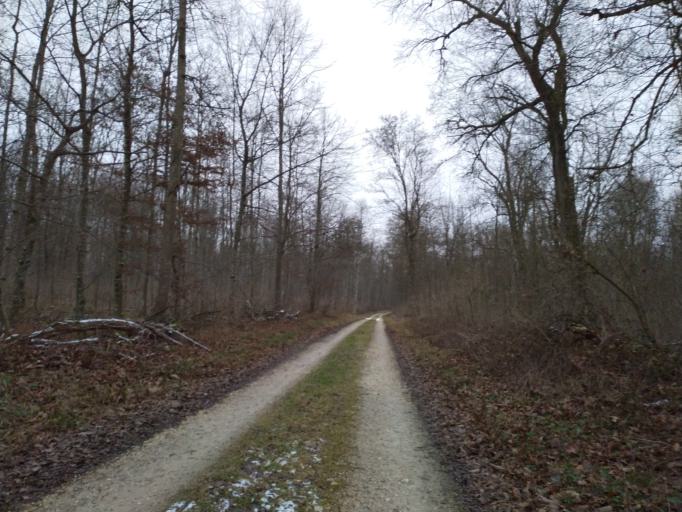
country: DE
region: Bavaria
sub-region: Swabia
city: Offingen
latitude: 48.4893
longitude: 10.3363
